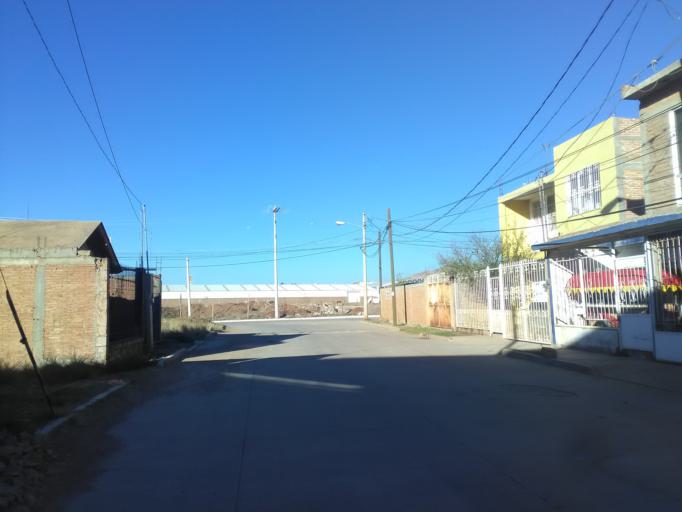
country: MX
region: Durango
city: Victoria de Durango
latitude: 24.0542
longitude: -104.6496
